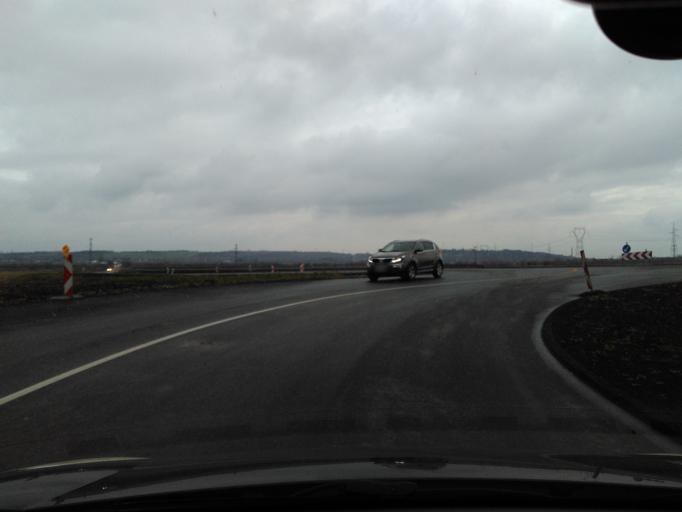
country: HU
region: Heves
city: Hatvan
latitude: 47.6949
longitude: 19.6670
